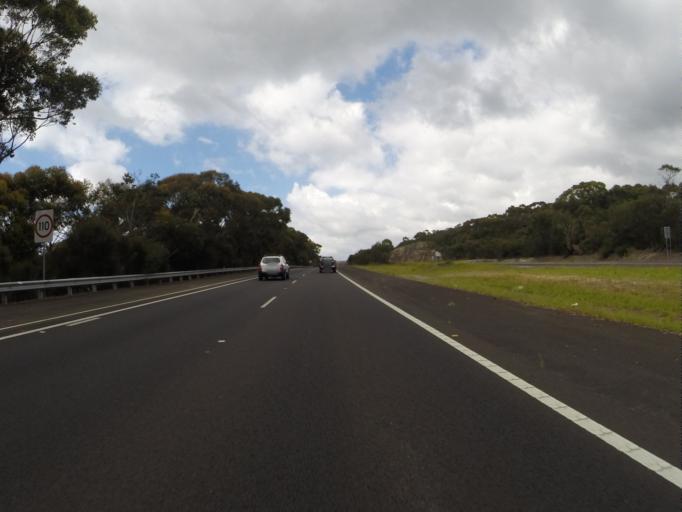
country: AU
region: New South Wales
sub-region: Wollongong
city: Helensburgh
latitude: -34.2081
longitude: 150.9628
